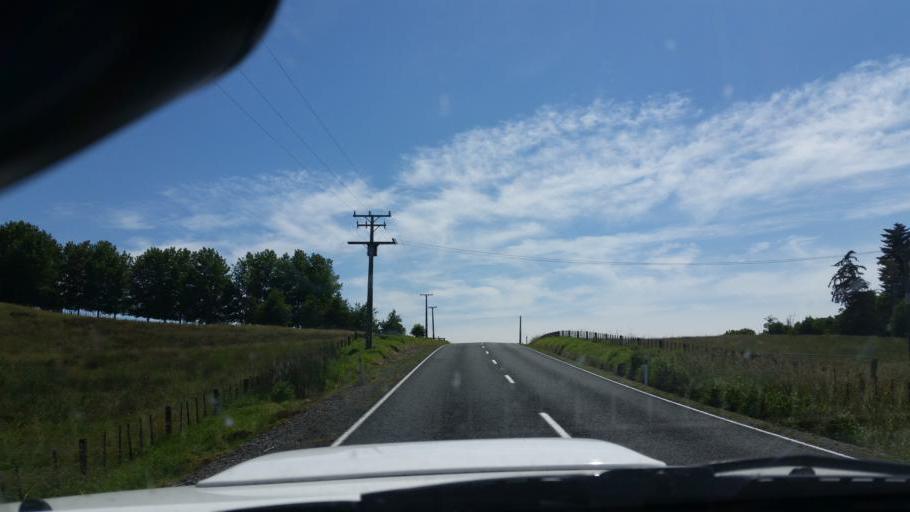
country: NZ
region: Auckland
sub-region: Auckland
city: Wellsford
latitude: -36.1892
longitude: 174.4073
